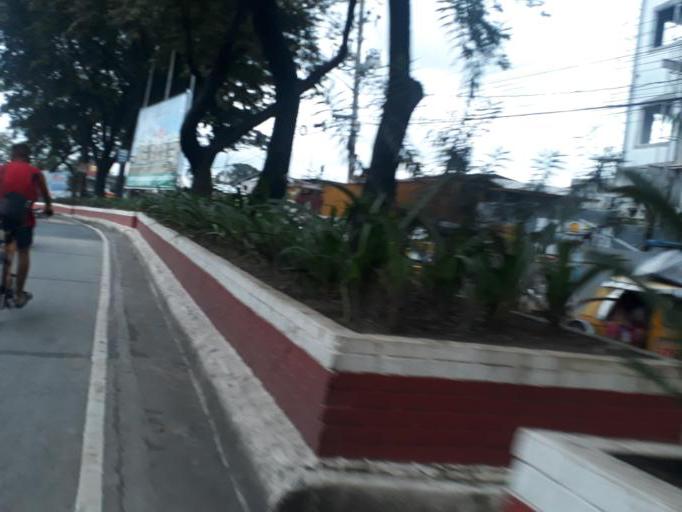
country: PH
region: Calabarzon
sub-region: Province of Rizal
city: San Mateo
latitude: 14.6863
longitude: 121.0891
